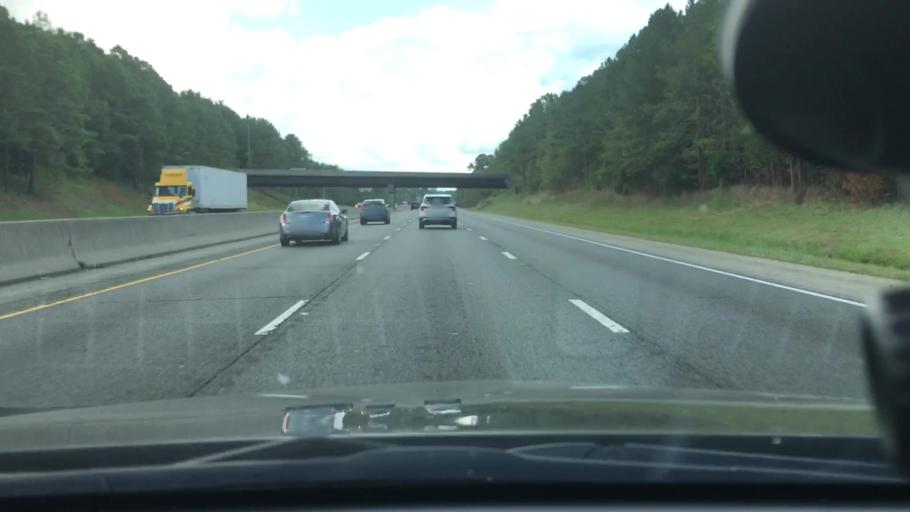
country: US
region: North Carolina
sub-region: Orange County
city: Chapel Hill
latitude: 35.9348
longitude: -78.9898
